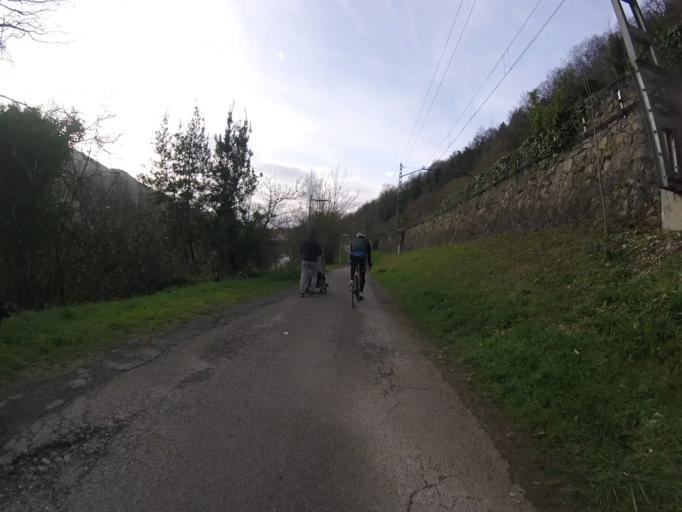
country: ES
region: Basque Country
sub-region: Provincia de Guipuzcoa
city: Irura
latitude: 43.1678
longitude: -2.0712
